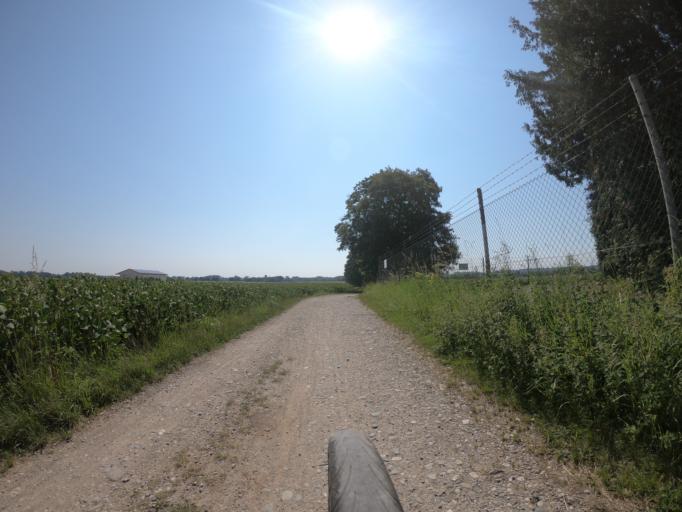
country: DE
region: Bavaria
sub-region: Upper Bavaria
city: Emmering
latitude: 48.1982
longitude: 11.2848
